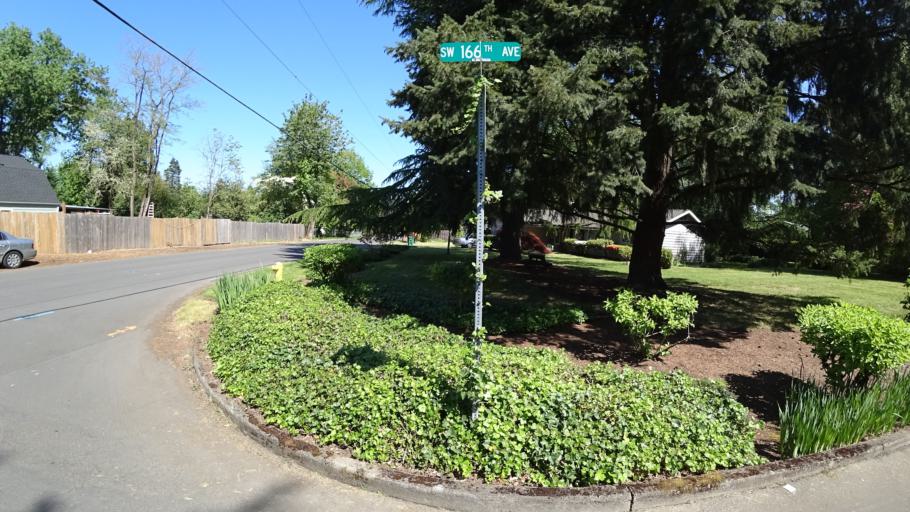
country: US
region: Oregon
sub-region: Washington County
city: Aloha
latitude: 45.4809
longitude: -122.8479
